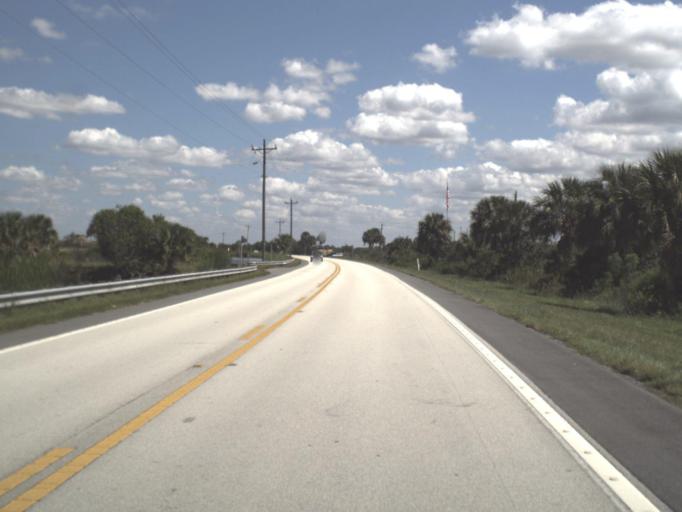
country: US
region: Florida
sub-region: Collier County
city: Marco
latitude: 25.9021
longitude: -81.3388
